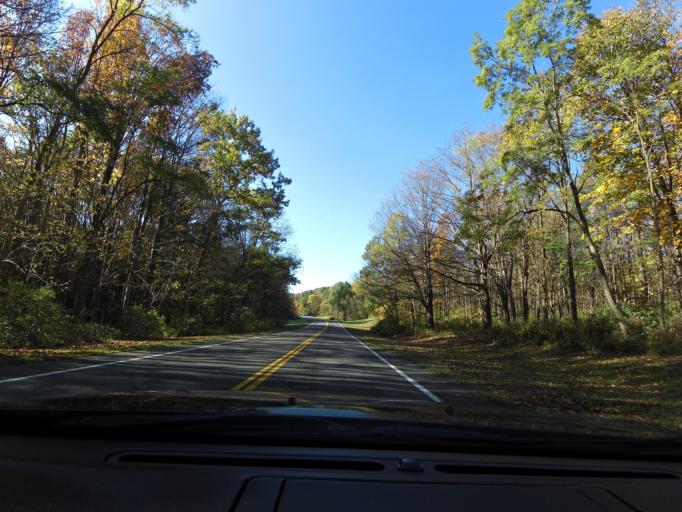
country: US
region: New York
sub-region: Wyoming County
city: Perry
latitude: 42.6930
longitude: -77.9589
